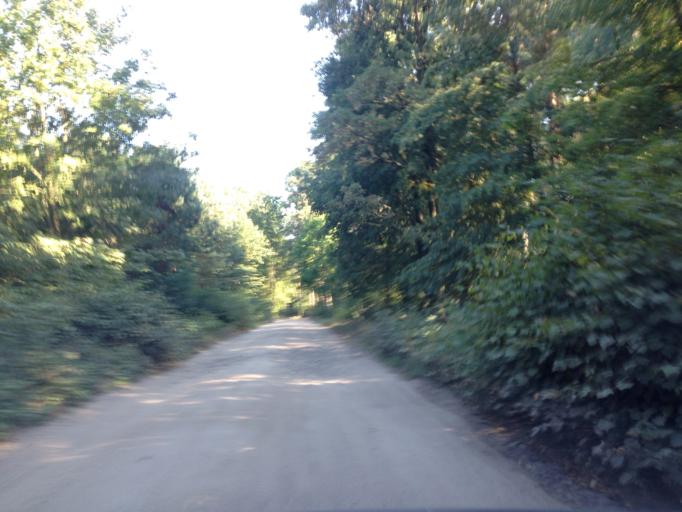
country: PL
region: Kujawsko-Pomorskie
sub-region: Powiat brodnicki
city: Gorzno
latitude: 53.1806
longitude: 19.6489
